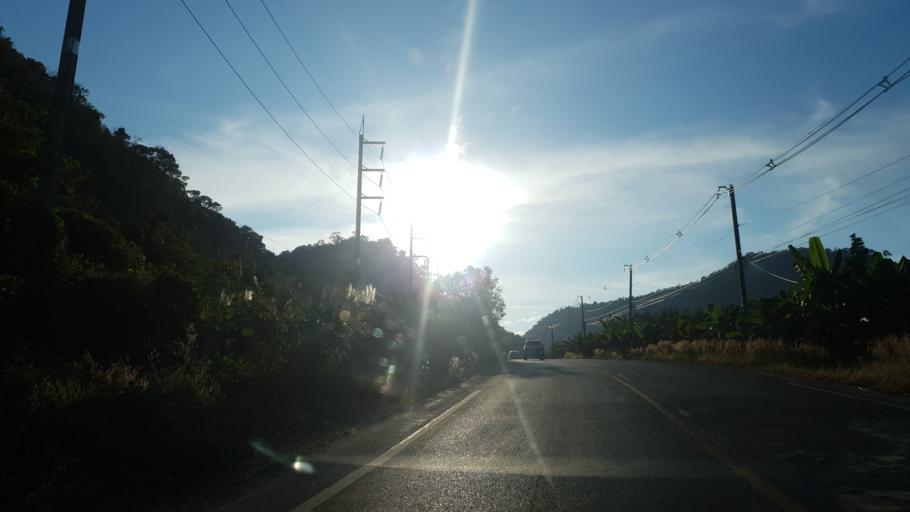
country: TH
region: Loei
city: Dan Sai
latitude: 17.2272
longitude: 101.0376
